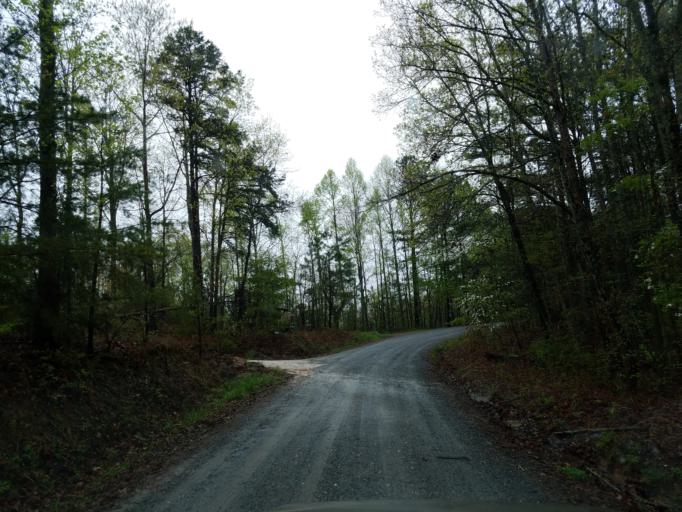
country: US
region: Georgia
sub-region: Pickens County
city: Jasper
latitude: 34.5501
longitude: -84.5238
